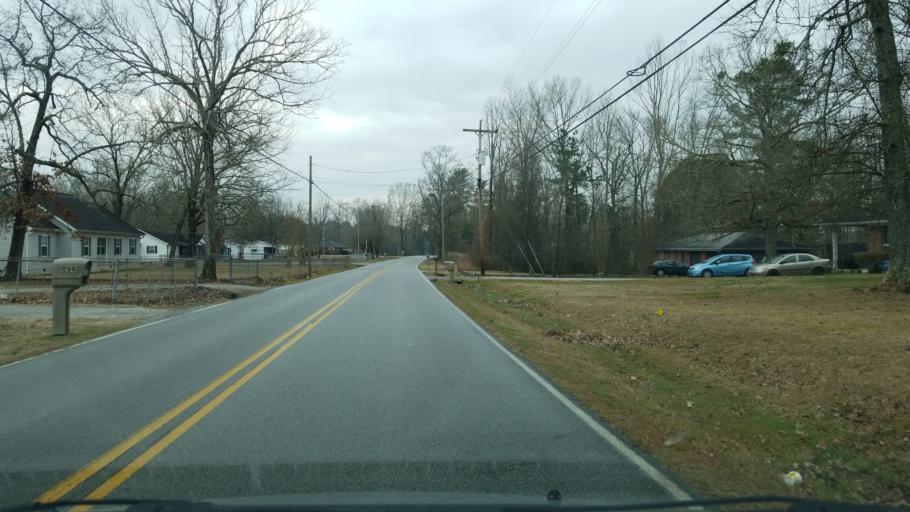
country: US
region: Georgia
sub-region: Catoosa County
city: Indian Springs
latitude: 34.9659
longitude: -85.1588
